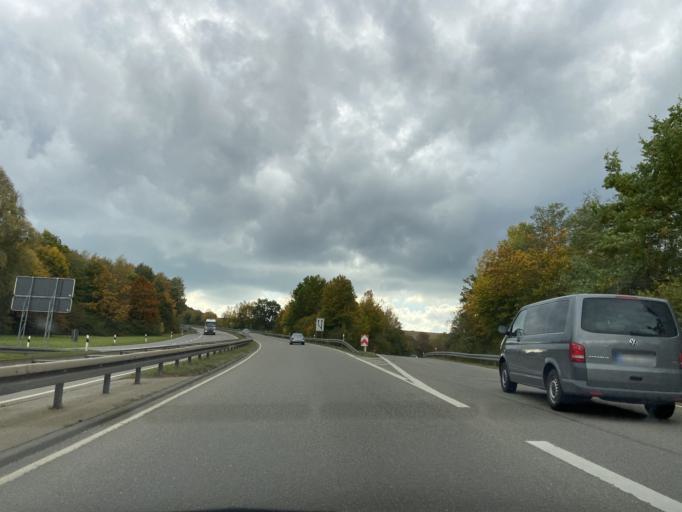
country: DE
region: Baden-Wuerttemberg
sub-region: Tuebingen Region
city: Sigmaringen
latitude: 48.0774
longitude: 9.2063
